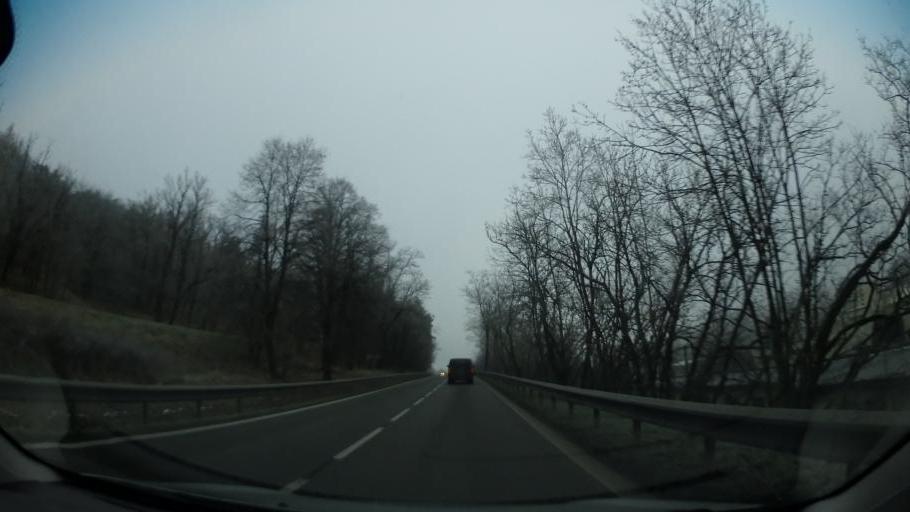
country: CZ
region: Vysocina
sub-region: Okres Trebic
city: Trebic
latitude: 49.2155
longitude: 15.9137
